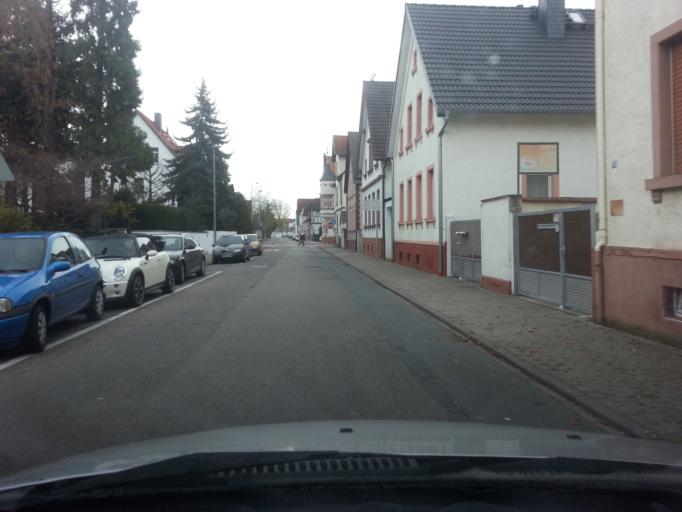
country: DE
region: Hesse
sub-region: Regierungsbezirk Darmstadt
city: Gross-Gerau
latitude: 49.9197
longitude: 8.4808
